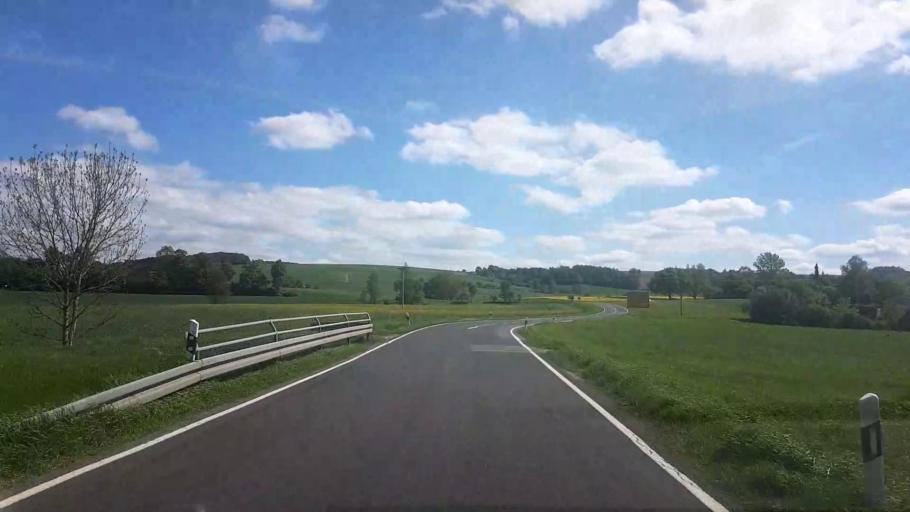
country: DE
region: Bavaria
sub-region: Regierungsbezirk Unterfranken
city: Untermerzbach
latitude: 50.1292
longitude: 10.8844
